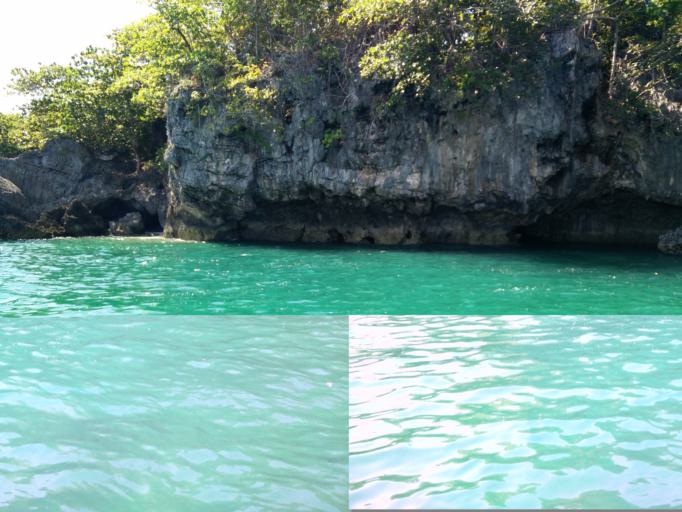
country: MM
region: Ayeyarwady
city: Pathein
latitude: 16.8491
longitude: 94.2727
